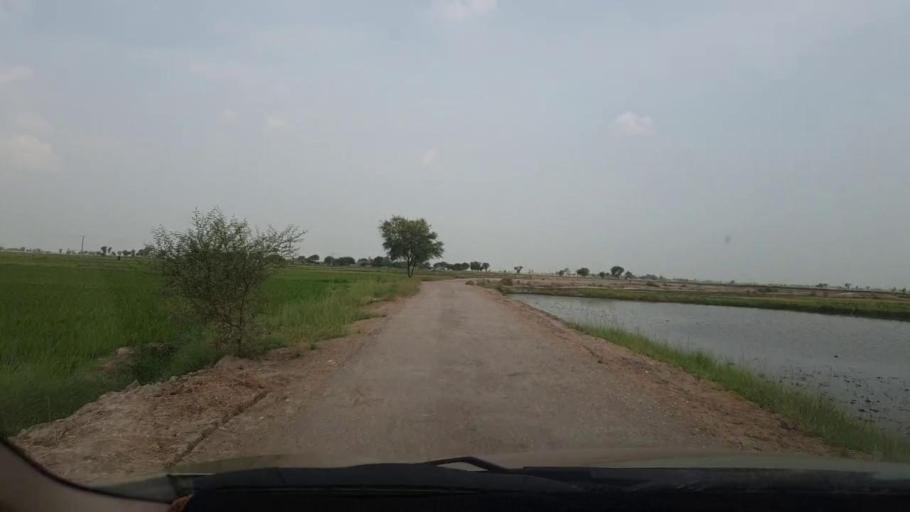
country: PK
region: Sindh
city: Larkana
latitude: 27.5143
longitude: 68.1307
